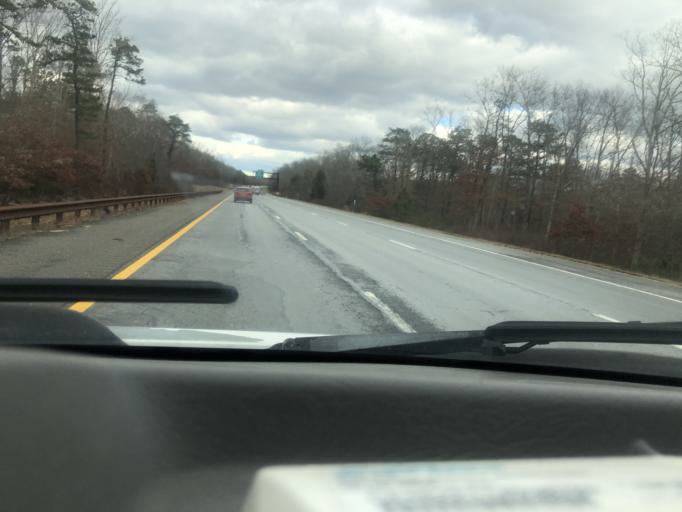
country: US
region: New Jersey
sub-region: Ocean County
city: Ocean Acres
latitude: 39.7265
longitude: -74.2670
